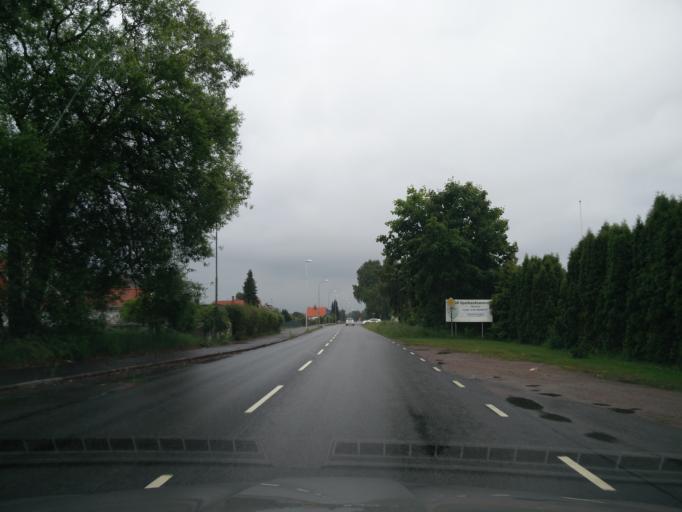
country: SE
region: Skane
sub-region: Hassleholms Kommun
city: Vinslov
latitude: 56.1014
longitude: 13.8952
